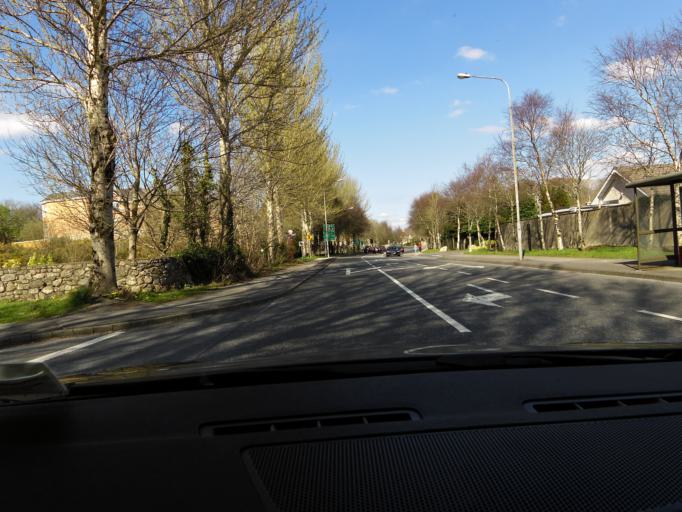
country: IE
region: Connaught
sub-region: County Galway
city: Gaillimh
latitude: 53.2881
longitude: -9.0748
